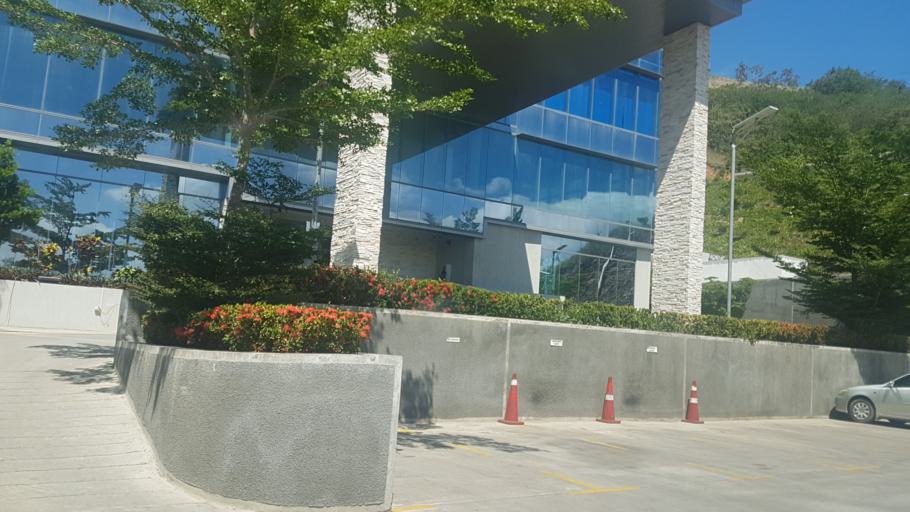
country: PG
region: National Capital
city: Port Moresby
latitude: -9.4403
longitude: 147.1773
